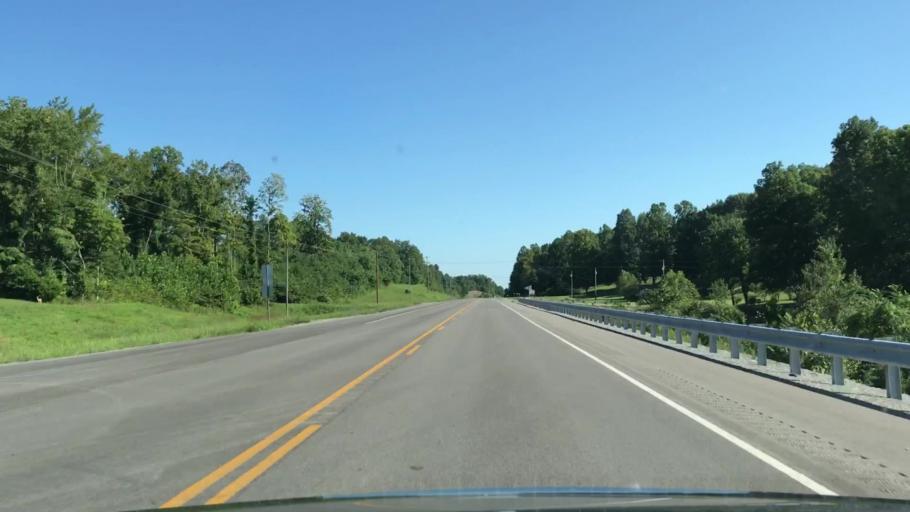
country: US
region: Kentucky
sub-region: Cumberland County
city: Burkesville
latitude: 36.6976
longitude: -85.3728
